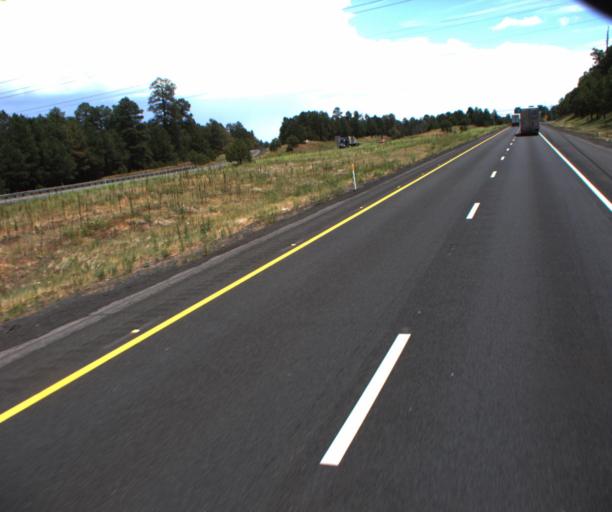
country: US
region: Arizona
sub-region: Coconino County
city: Flagstaff
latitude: 35.1926
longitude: -111.7330
